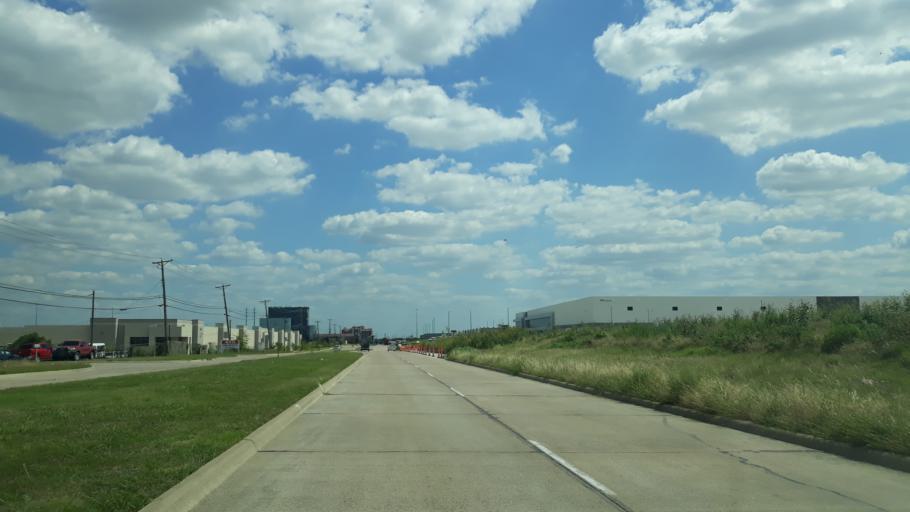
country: US
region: Texas
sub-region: Tarrant County
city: Euless
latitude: 32.8472
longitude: -97.0219
